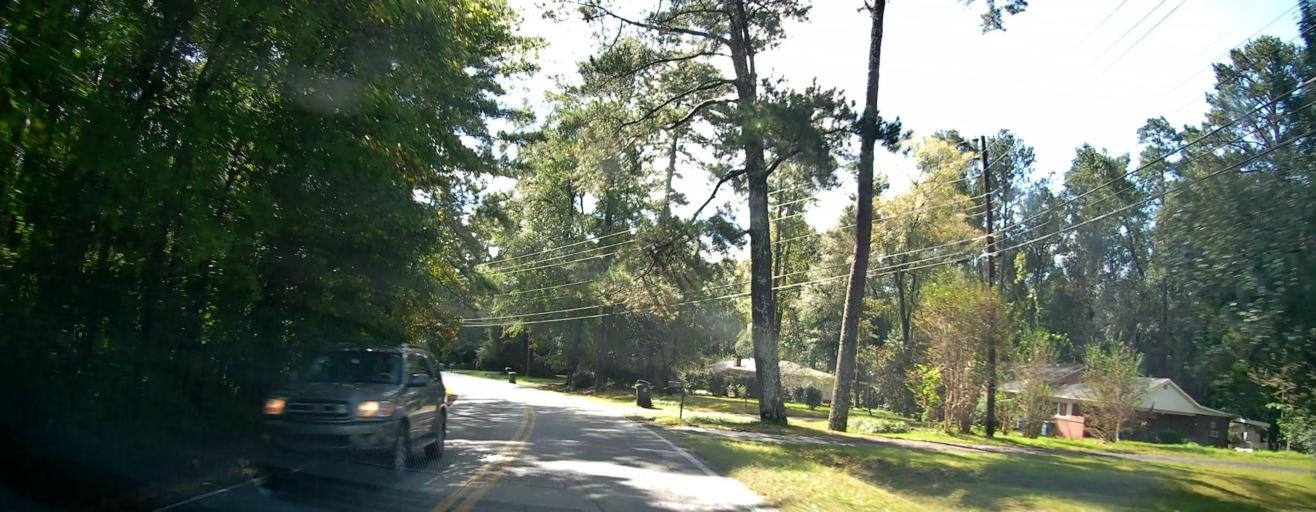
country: US
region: Georgia
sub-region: Bibb County
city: Macon
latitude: 32.9152
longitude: -83.7205
